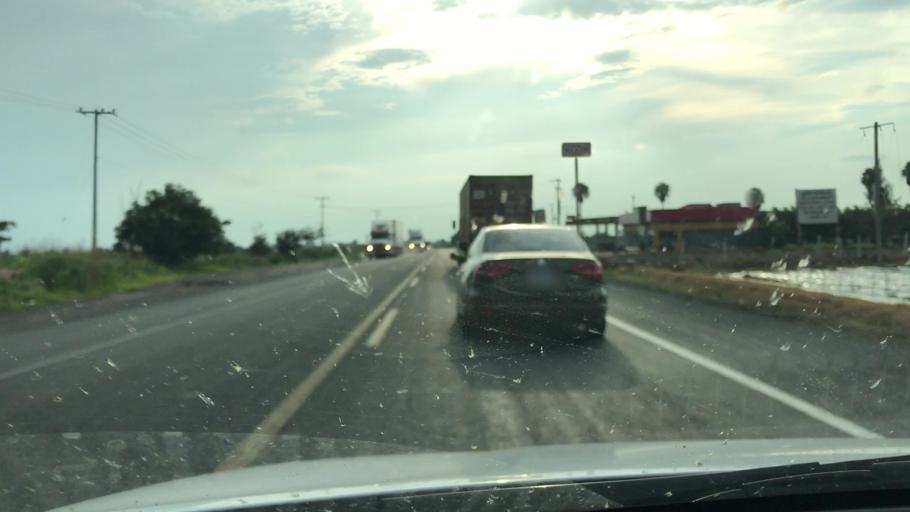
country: MX
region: Michoacan
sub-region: Yurecuaro
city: Yurecuaro
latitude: 20.3281
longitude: -102.2615
